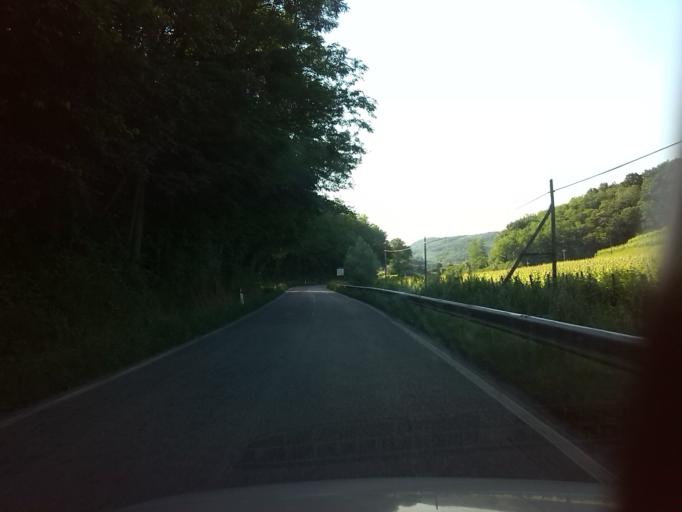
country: IT
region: Friuli Venezia Giulia
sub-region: Provincia di Udine
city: Prepotto
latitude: 46.0463
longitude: 13.4689
